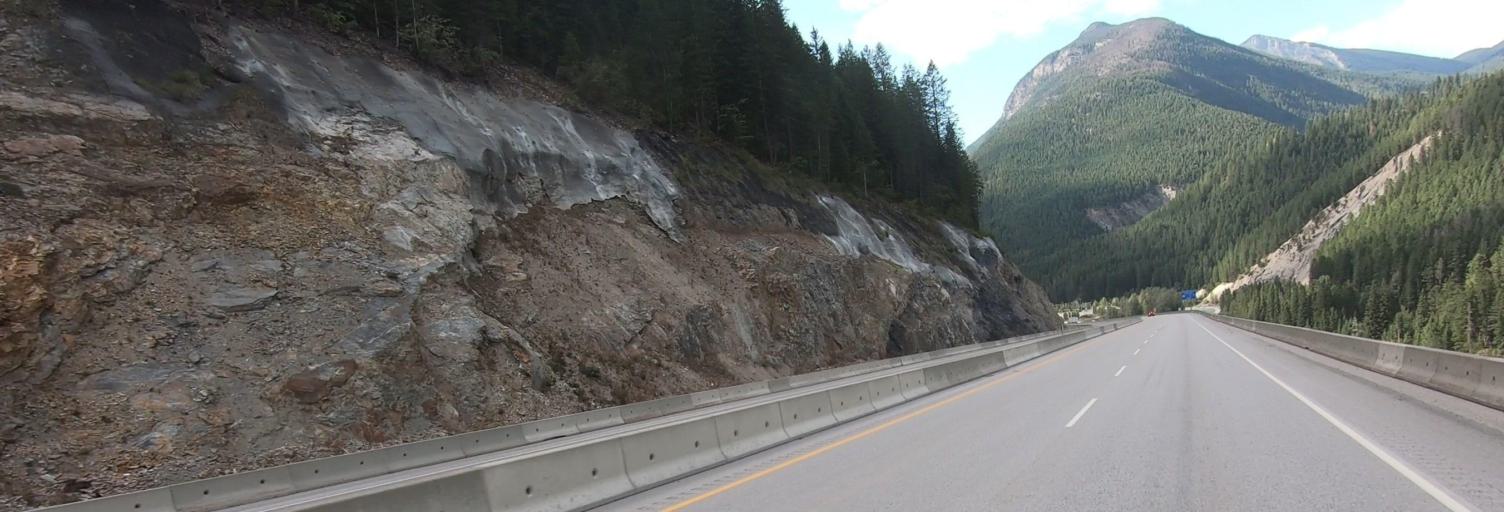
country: CA
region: British Columbia
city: Golden
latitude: 51.2820
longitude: -116.8158
